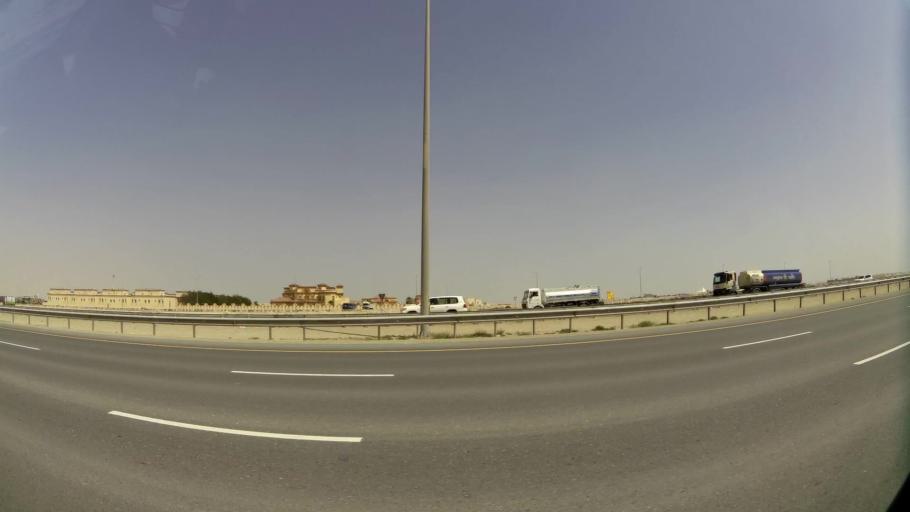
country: QA
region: Baladiyat Umm Salal
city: Umm Salal Muhammad
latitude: 25.4314
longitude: 51.4139
